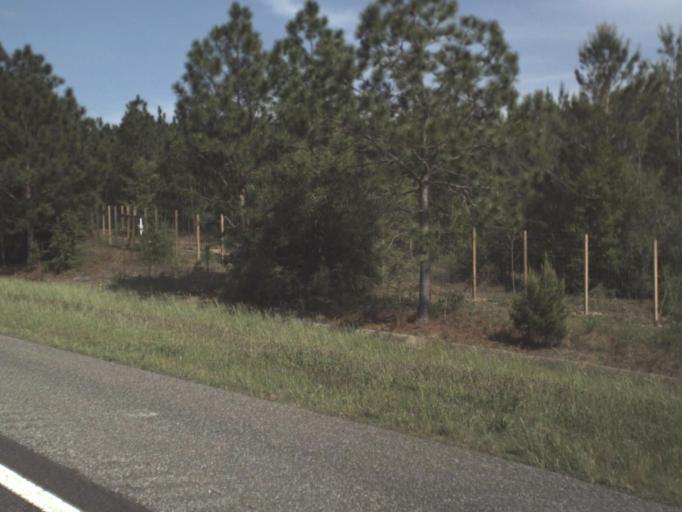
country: US
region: Florida
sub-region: Santa Rosa County
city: East Milton
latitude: 30.6837
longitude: -86.7971
